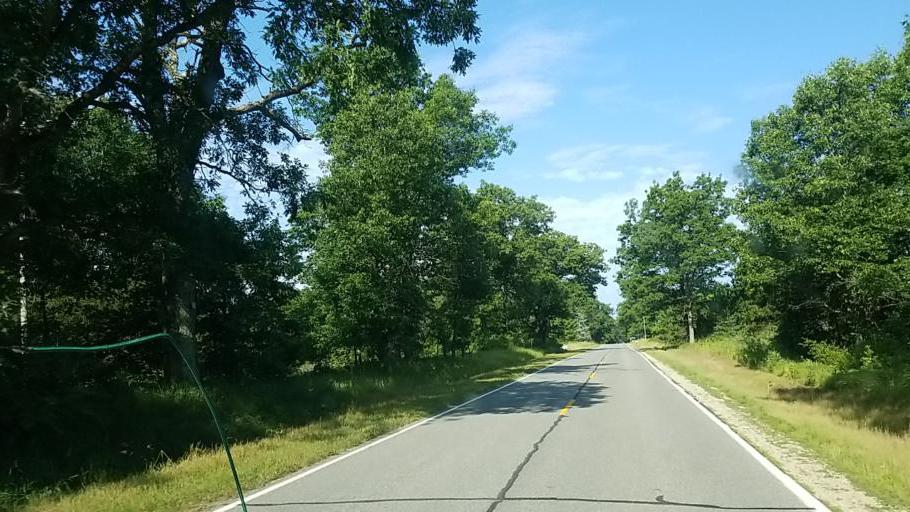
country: US
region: Michigan
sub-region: Muskegon County
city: Twin Lake
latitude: 43.4688
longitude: -86.1725
